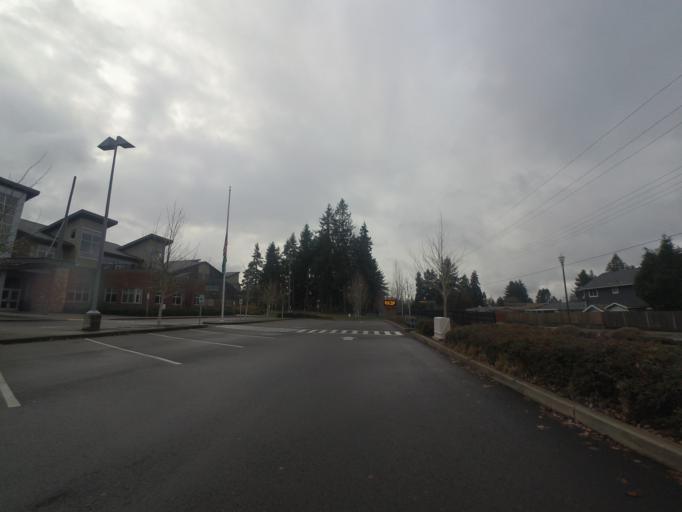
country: US
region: Washington
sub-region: Pierce County
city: University Place
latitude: 47.2240
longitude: -122.5538
